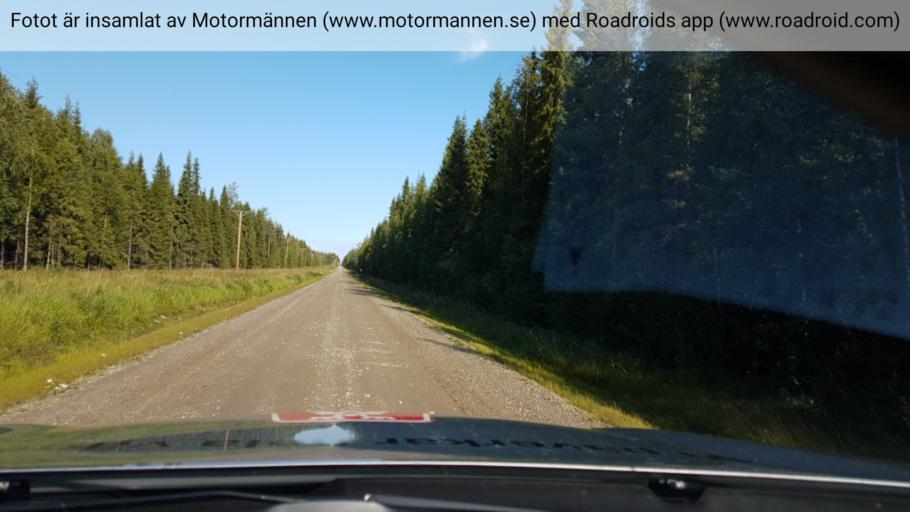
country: SE
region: Norrbotten
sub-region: Kalix Kommun
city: Kalix
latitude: 66.1624
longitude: 23.2204
